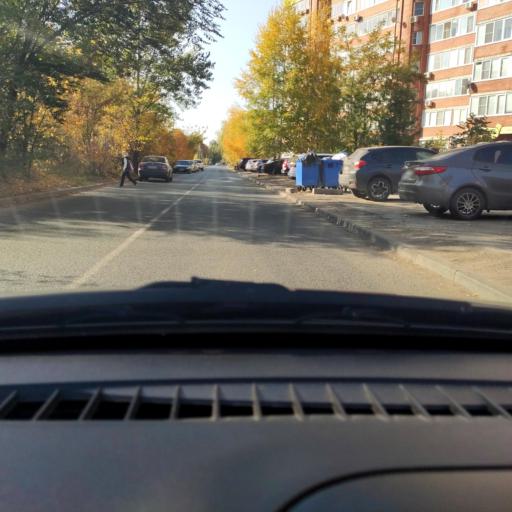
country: RU
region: Samara
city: Tol'yatti
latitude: 53.5186
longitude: 49.3162
